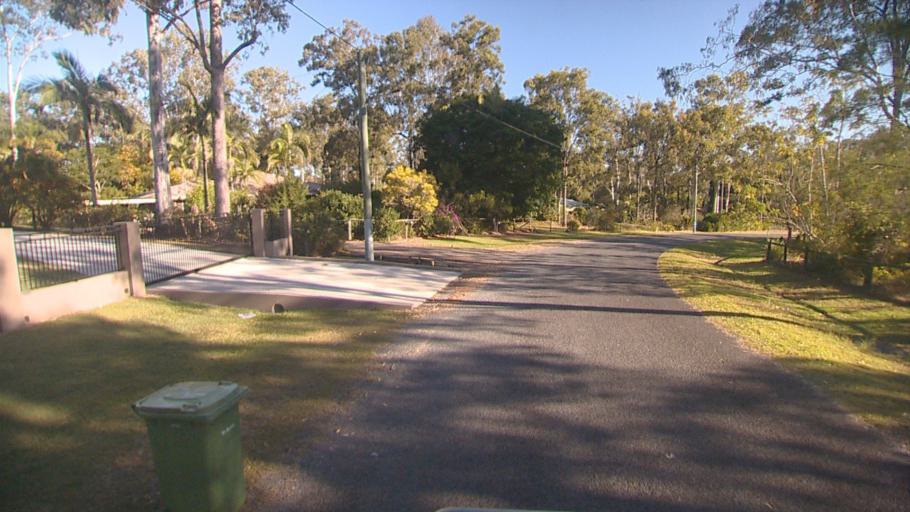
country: AU
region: Queensland
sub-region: Logan
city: Park Ridge South
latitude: -27.7455
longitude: 153.0238
